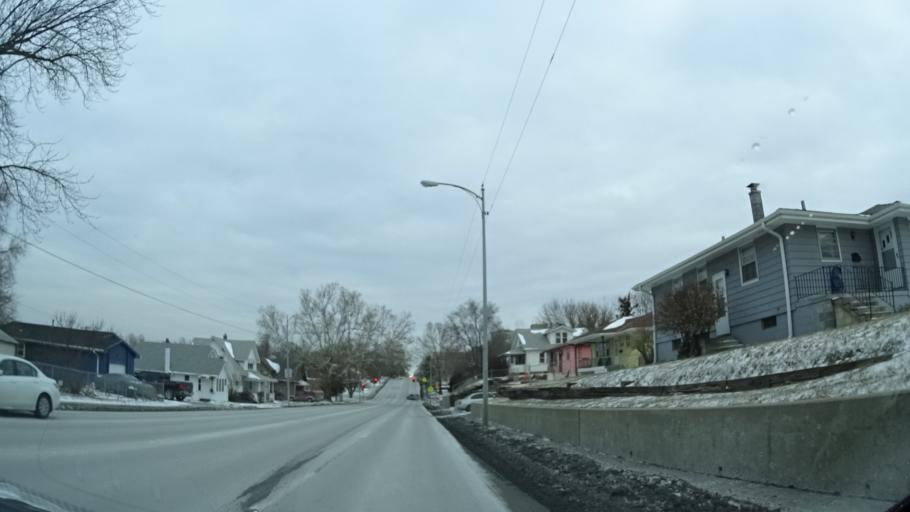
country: US
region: Nebraska
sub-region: Douglas County
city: Omaha
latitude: 41.2371
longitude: -95.9758
